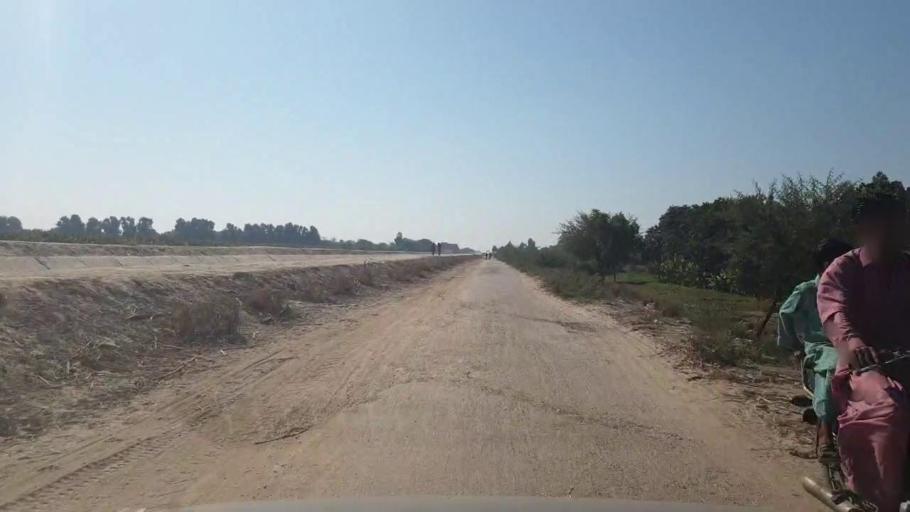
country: PK
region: Sindh
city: Mirwah Gorchani
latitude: 25.3018
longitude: 69.1029
